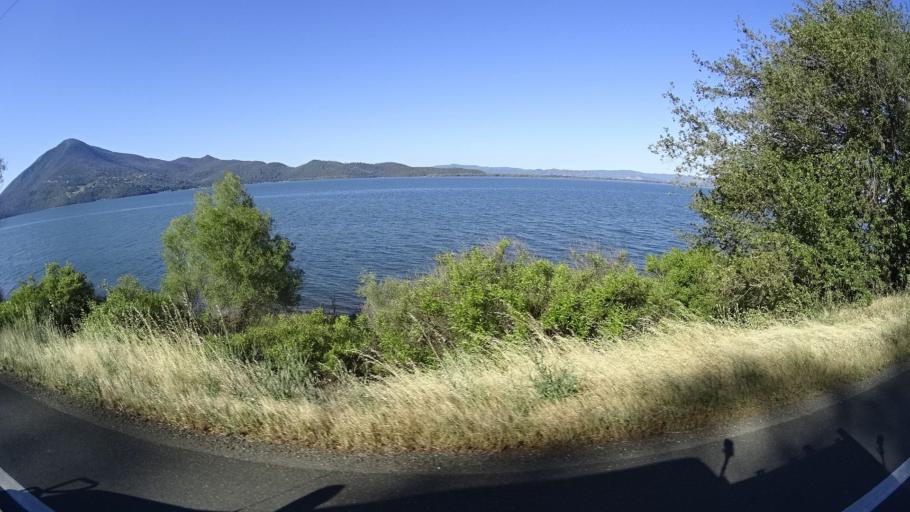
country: US
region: California
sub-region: Lake County
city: Soda Bay
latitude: 39.0420
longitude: -122.7750
